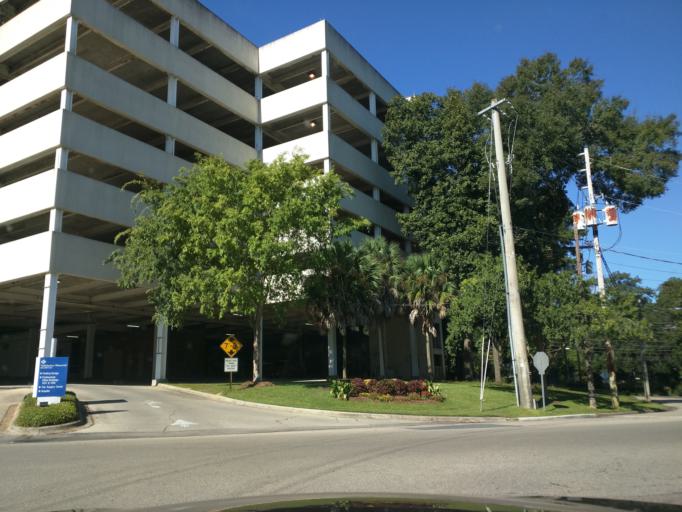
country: US
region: Florida
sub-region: Leon County
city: Tallahassee
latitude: 30.4590
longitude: -84.2610
